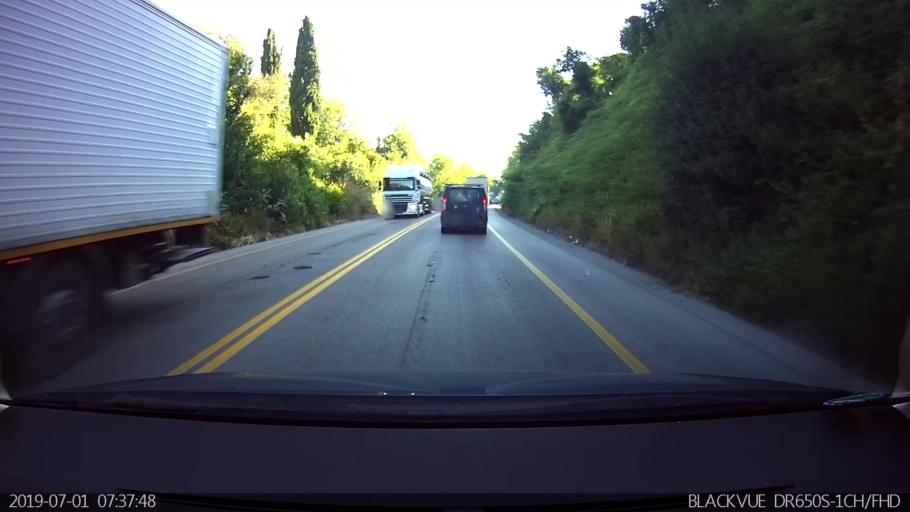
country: IT
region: Latium
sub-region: Provincia di Frosinone
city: Giuliano di Roma
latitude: 41.5403
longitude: 13.2673
